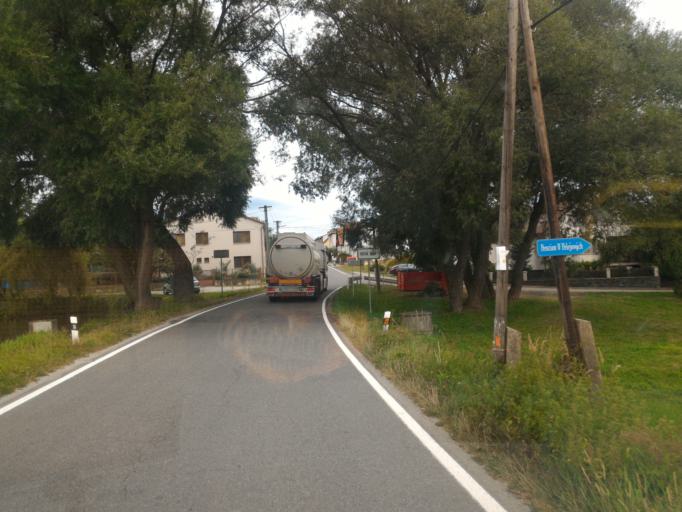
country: CZ
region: Vysocina
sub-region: Okres Jihlava
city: Telc
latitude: 49.1356
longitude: 15.5561
